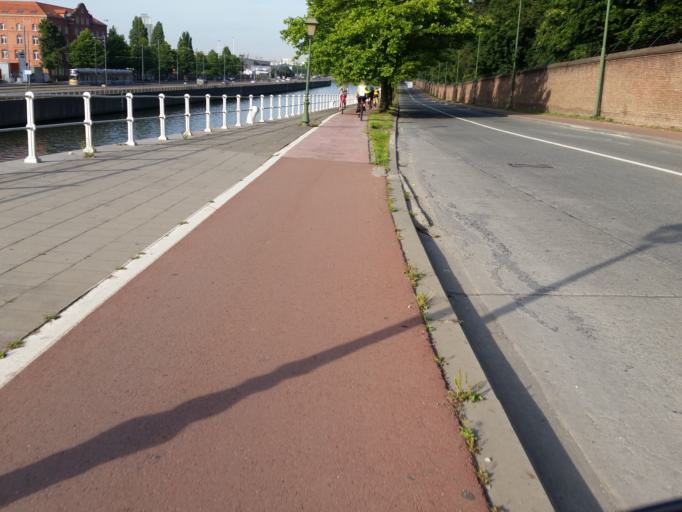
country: BE
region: Brussels Capital
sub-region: Bruxelles-Capitale
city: Brussels
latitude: 50.8809
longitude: 4.3725
